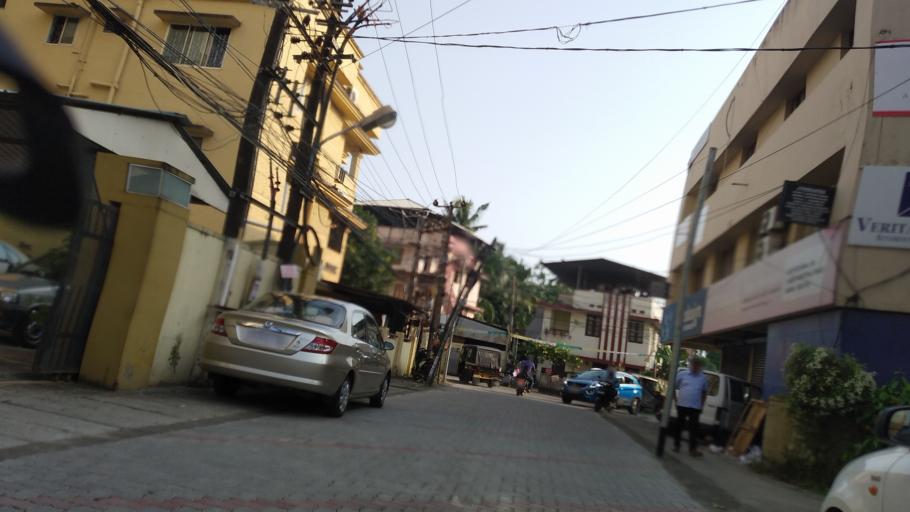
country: IN
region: Kerala
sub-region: Ernakulam
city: Cochin
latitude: 9.9866
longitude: 76.2892
